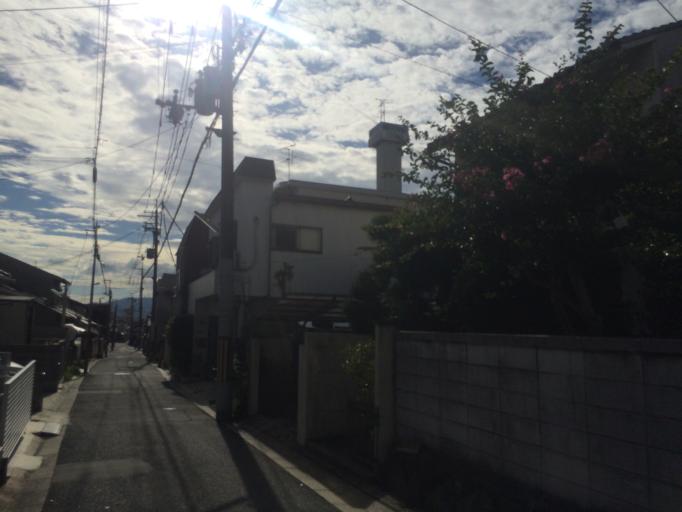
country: JP
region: Nara
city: Nara-shi
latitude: 34.6724
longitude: 135.8302
